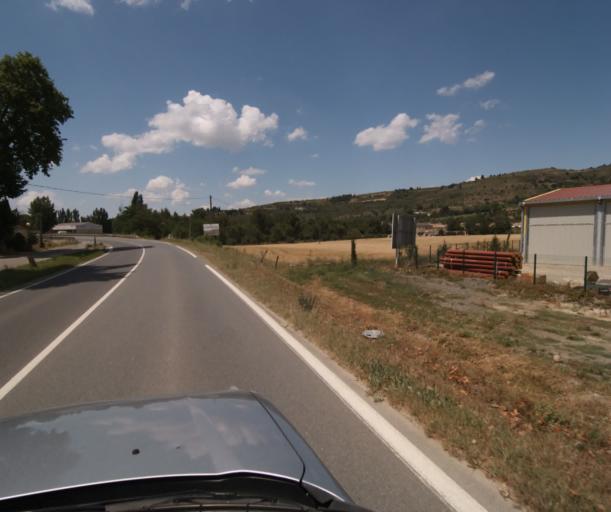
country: FR
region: Languedoc-Roussillon
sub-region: Departement de l'Aude
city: Limoux
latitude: 43.0427
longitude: 2.2395
